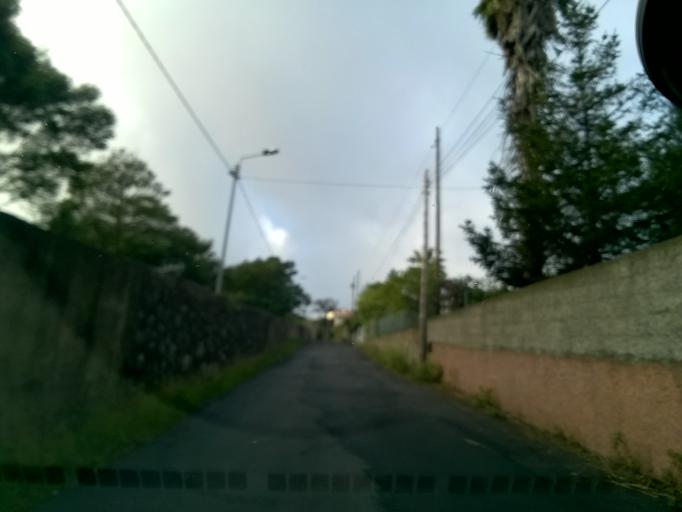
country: PT
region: Madeira
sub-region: Santa Cruz
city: Camacha
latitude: 32.6588
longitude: -16.8598
